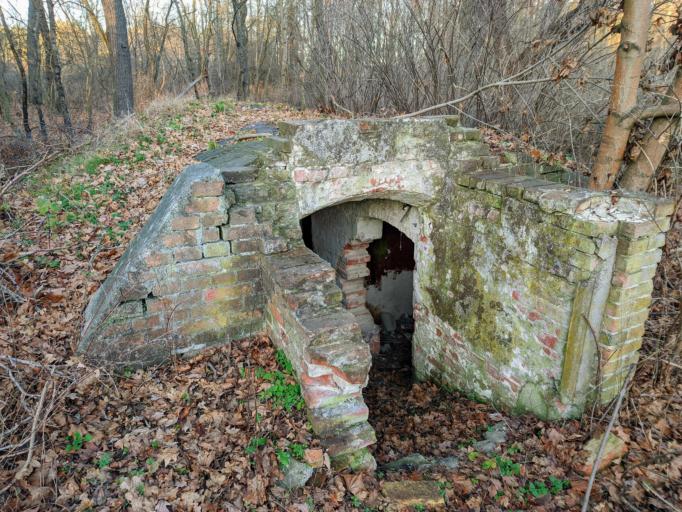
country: PL
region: Lubusz
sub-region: Powiat zaganski
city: Zagan
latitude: 51.5877
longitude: 15.3086
